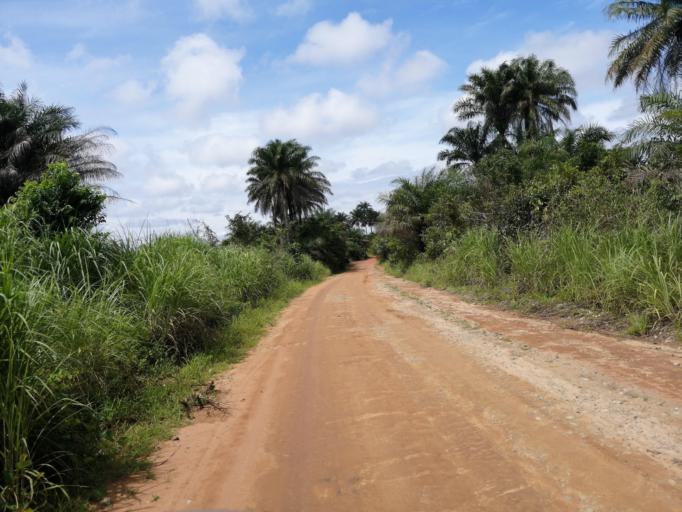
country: SL
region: Northern Province
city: Pepel
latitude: 8.6699
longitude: -13.0002
